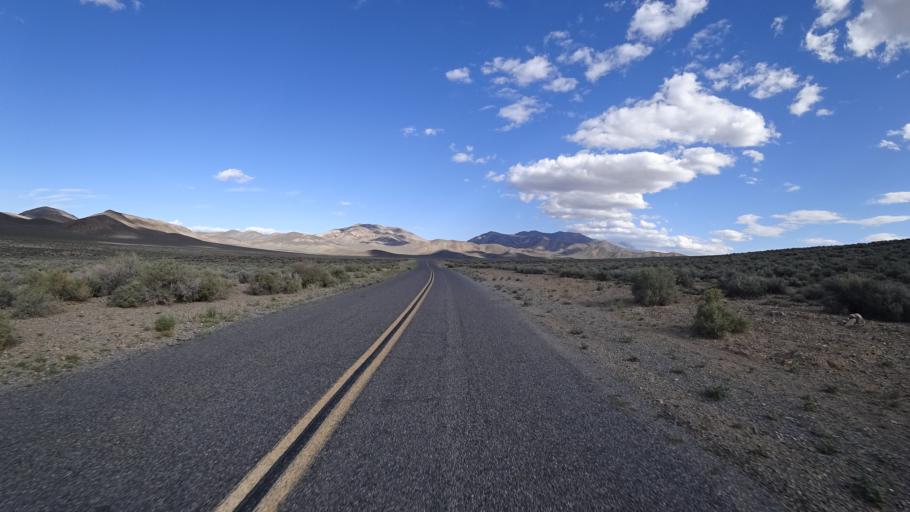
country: US
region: Nevada
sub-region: Nye County
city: Beatty
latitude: 36.3825
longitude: -117.1487
